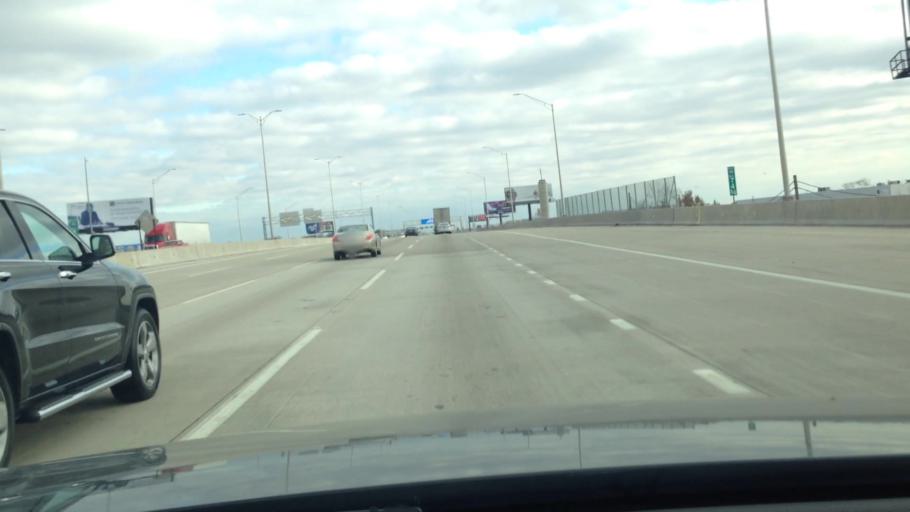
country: US
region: Illinois
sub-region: Cook County
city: Rosemont
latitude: 42.0129
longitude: -87.9201
